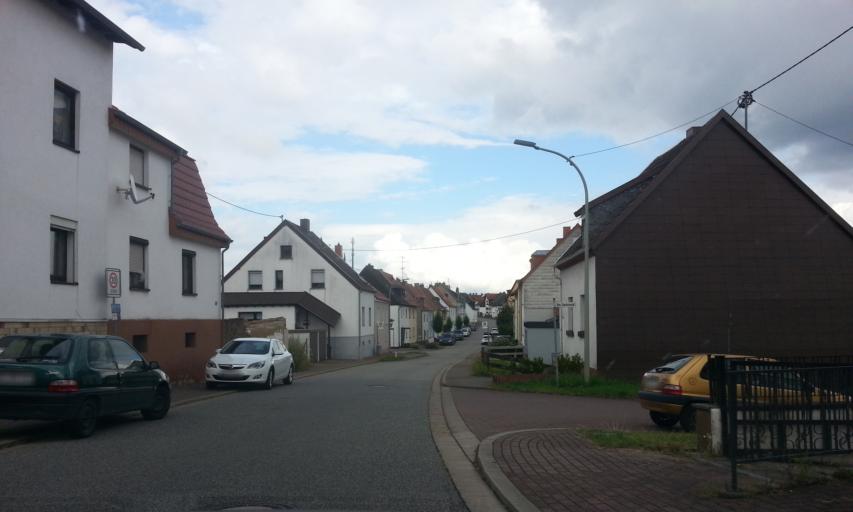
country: DE
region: Saarland
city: Schiffweiler
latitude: 49.3564
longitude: 7.1206
